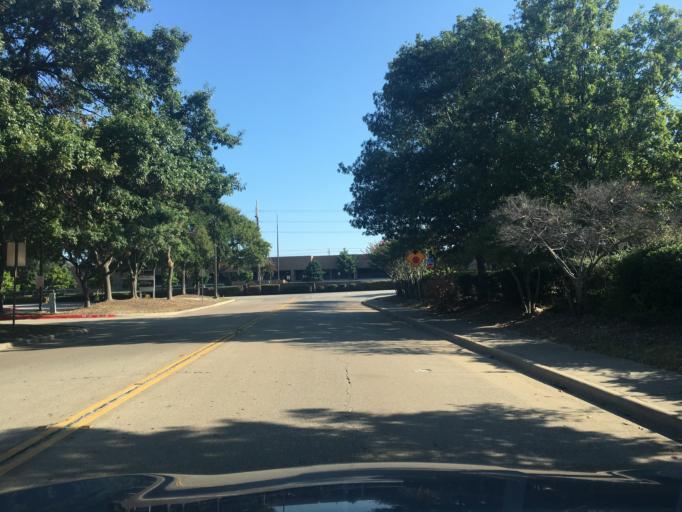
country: US
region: Texas
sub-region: Dallas County
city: Addison
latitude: 32.9551
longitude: -96.8514
